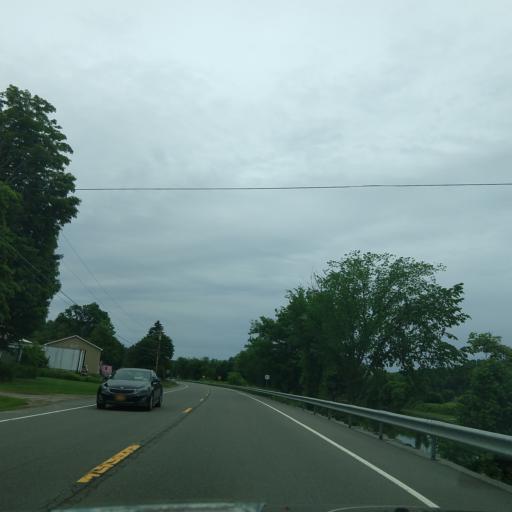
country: US
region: New York
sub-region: Cortland County
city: McGraw
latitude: 42.4543
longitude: -76.0430
